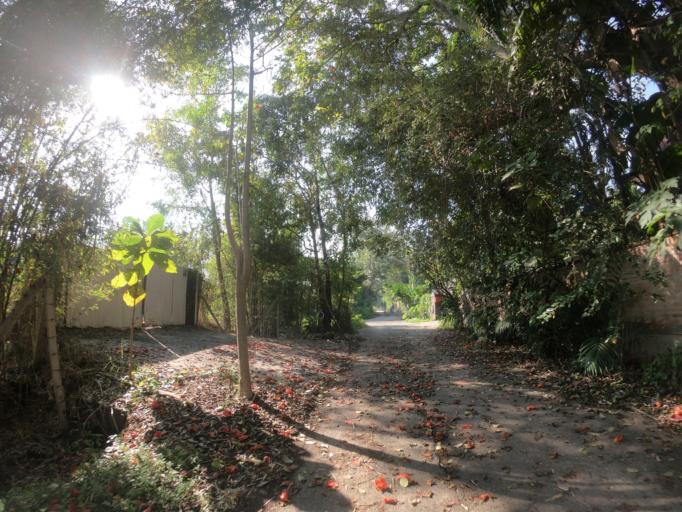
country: TH
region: Chiang Mai
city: Chiang Mai
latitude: 18.7501
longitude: 98.9834
